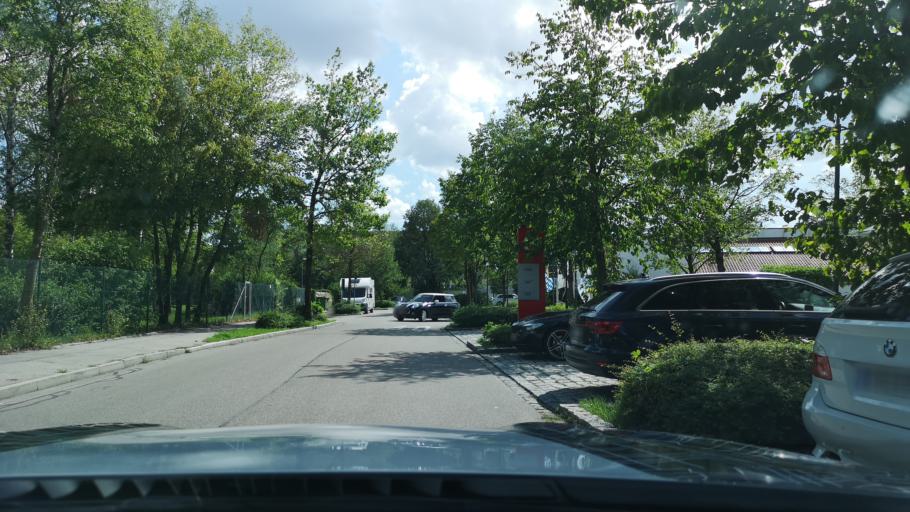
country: DE
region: Bavaria
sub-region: Upper Bavaria
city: Garching bei Munchen
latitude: 48.2487
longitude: 11.6127
